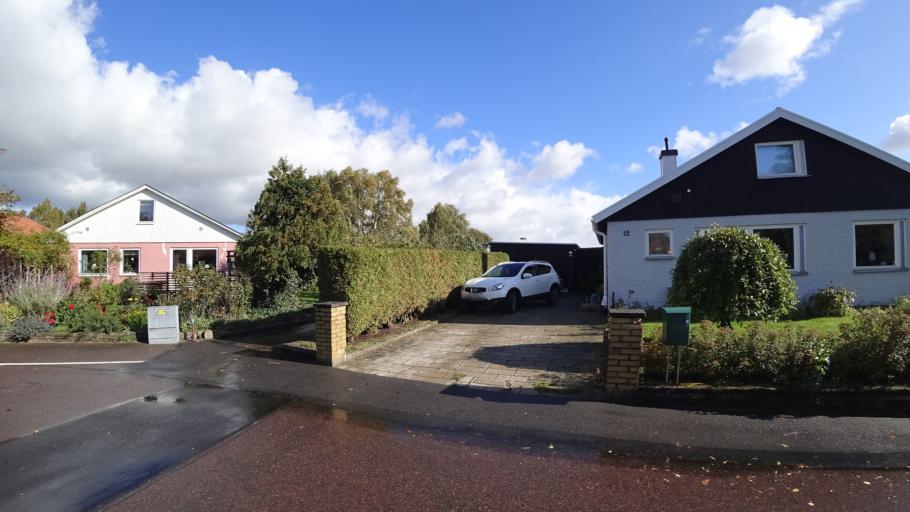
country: SE
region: Skane
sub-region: Kavlinge Kommun
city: Loddekopinge
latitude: 55.7559
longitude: 13.0031
